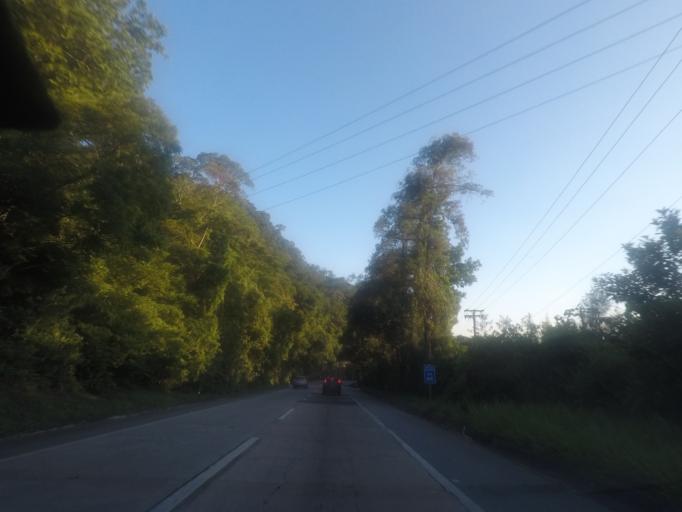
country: BR
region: Rio de Janeiro
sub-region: Petropolis
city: Petropolis
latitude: -22.5353
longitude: -43.2332
